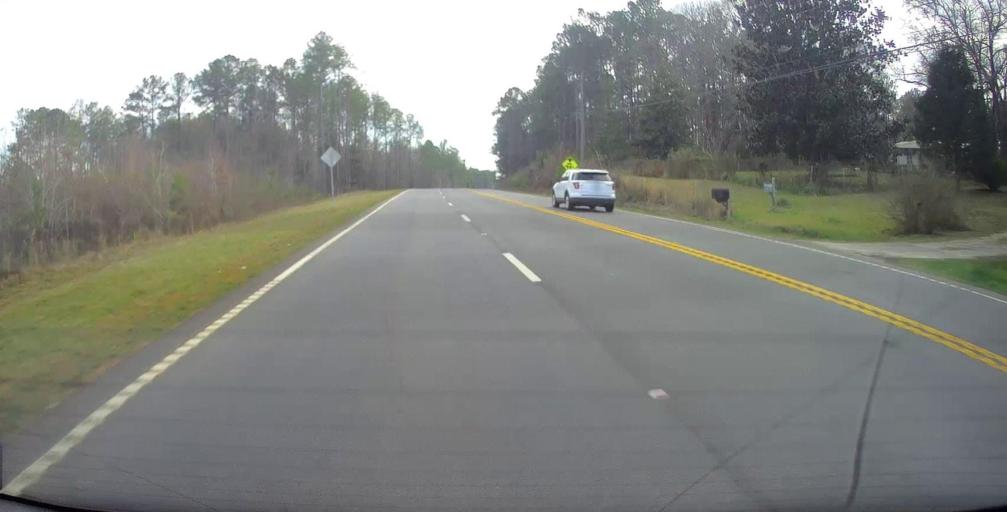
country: US
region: Georgia
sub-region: Harris County
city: Hamilton
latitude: 32.7184
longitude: -84.8730
